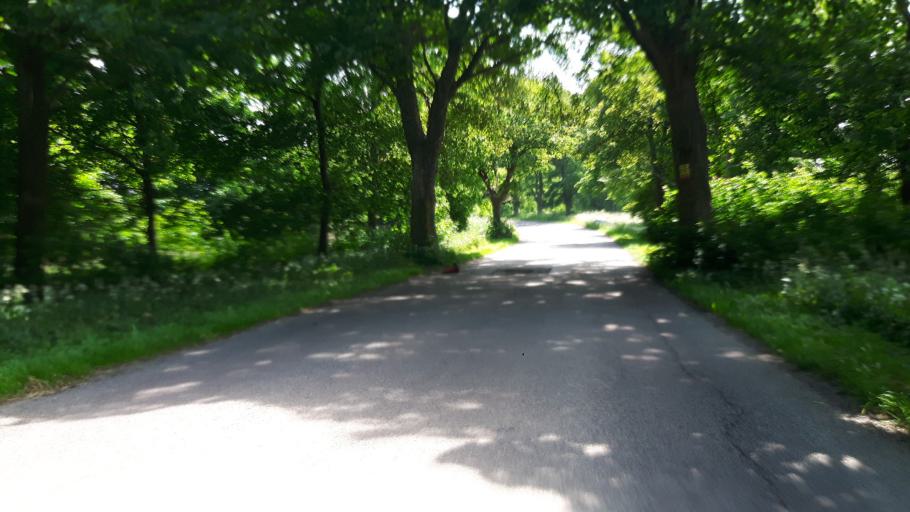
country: PL
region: Pomeranian Voivodeship
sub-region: Powiat wejherowski
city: Choczewo
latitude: 54.7407
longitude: 17.8151
